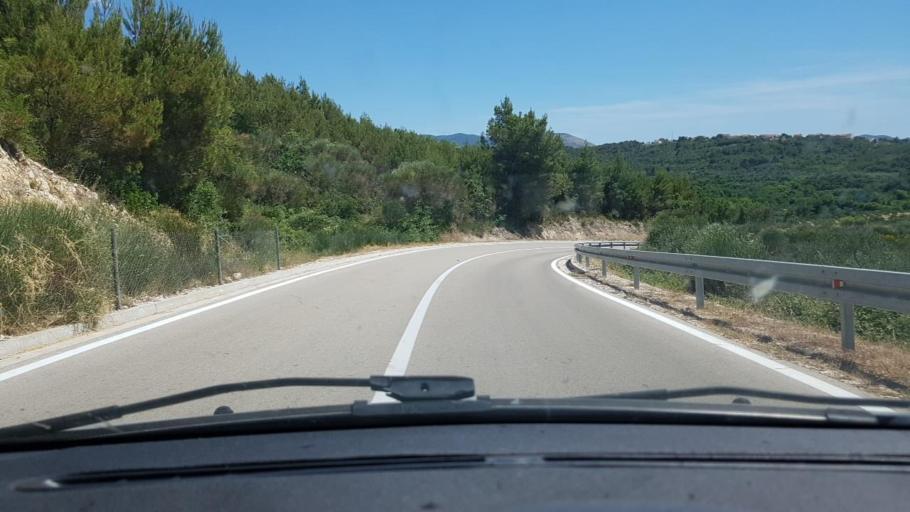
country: HR
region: Sibensko-Kniniska
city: Zaton
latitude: 43.8457
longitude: 15.9020
